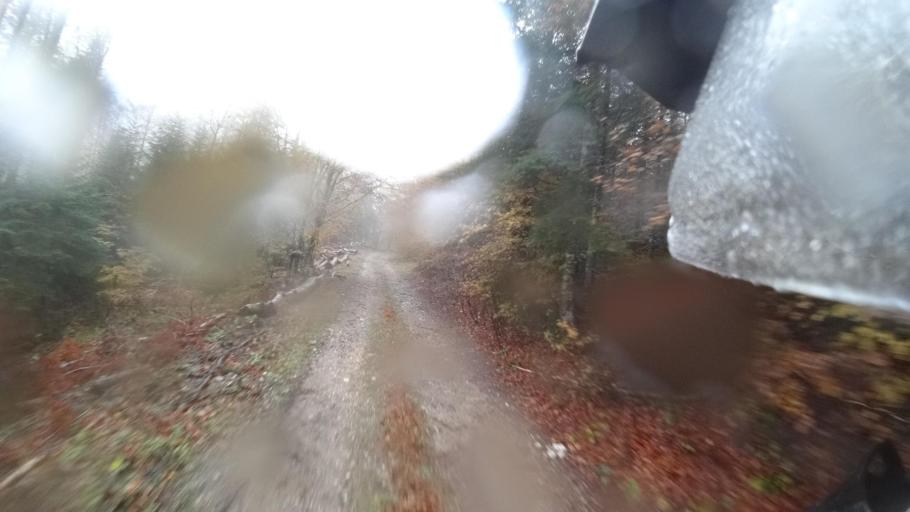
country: HR
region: Primorsko-Goranska
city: Vrbovsko
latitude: 45.2922
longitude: 14.9423
